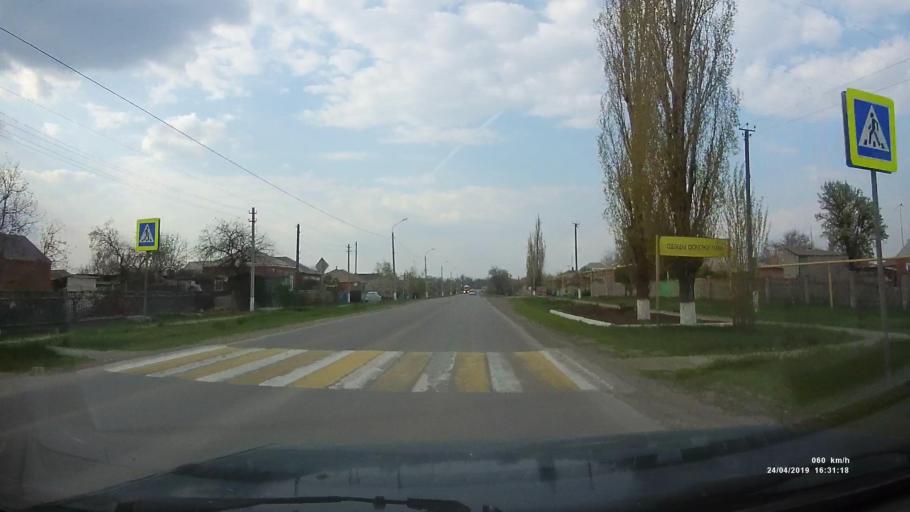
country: RU
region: Rostov
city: Orlovskiy
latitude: 46.8803
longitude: 42.0385
